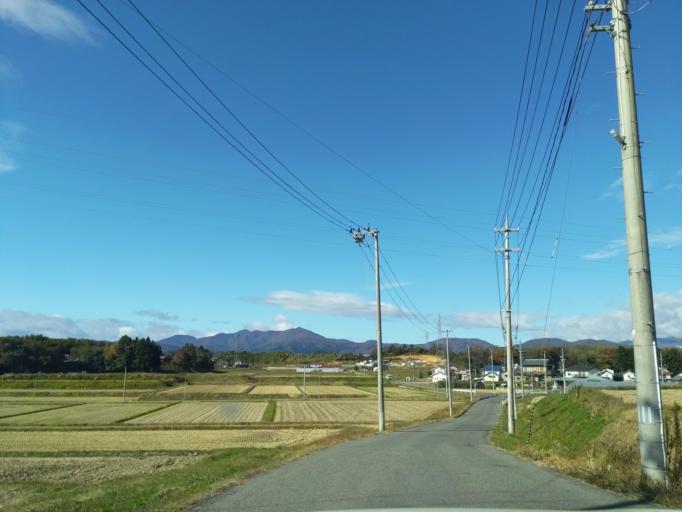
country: JP
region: Fukushima
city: Koriyama
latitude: 37.4419
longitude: 140.3275
